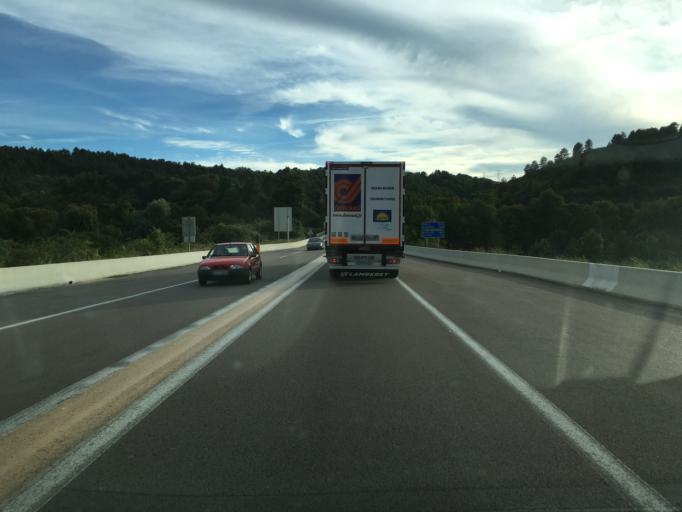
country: FR
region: Bourgogne
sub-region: Departement de la Cote-d'Or
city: Plombieres-les-Dijon
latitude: 47.3339
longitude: 4.9815
